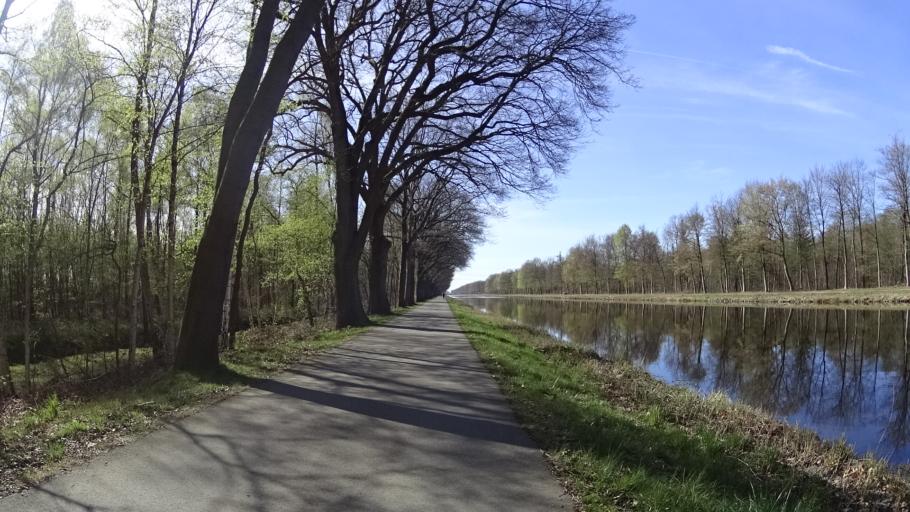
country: DE
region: Lower Saxony
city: Meppen
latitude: 52.6538
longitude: 7.3058
